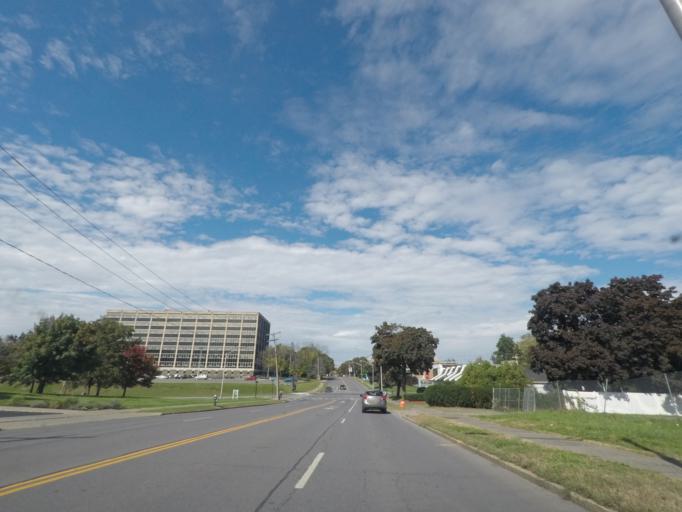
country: US
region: New York
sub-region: Albany County
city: Albany
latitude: 42.6466
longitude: -73.7722
